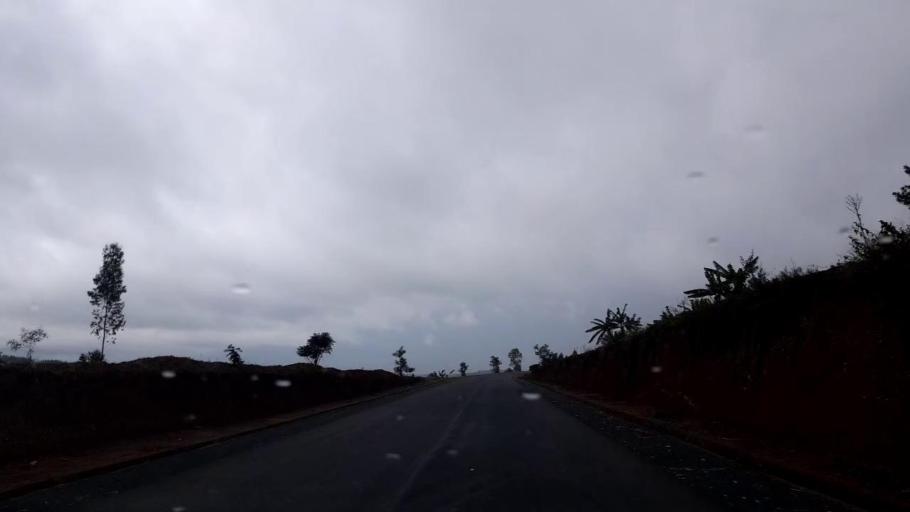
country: RW
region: Northern Province
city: Byumba
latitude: -1.4260
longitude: 30.2668
